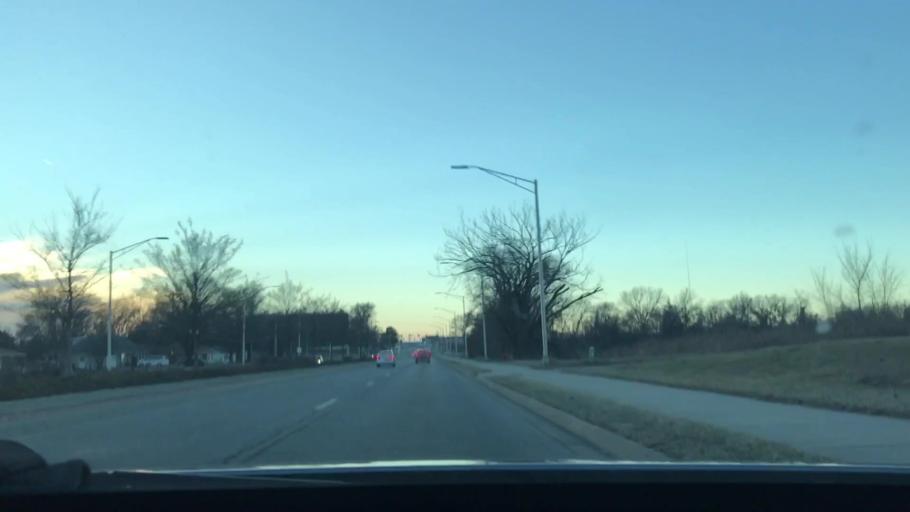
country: US
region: Kansas
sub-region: Wyandotte County
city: Edwardsville
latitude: 39.1165
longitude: -94.7936
